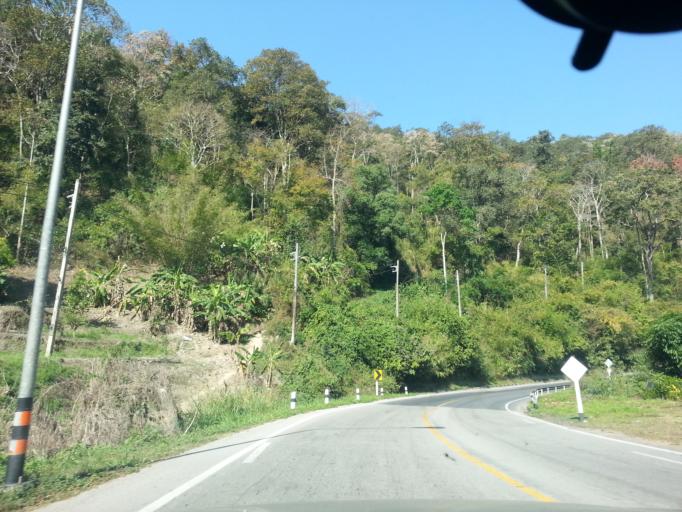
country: TH
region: Chiang Mai
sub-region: Amphoe Chiang Dao
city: Chiang Dao
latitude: 19.2481
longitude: 98.9678
